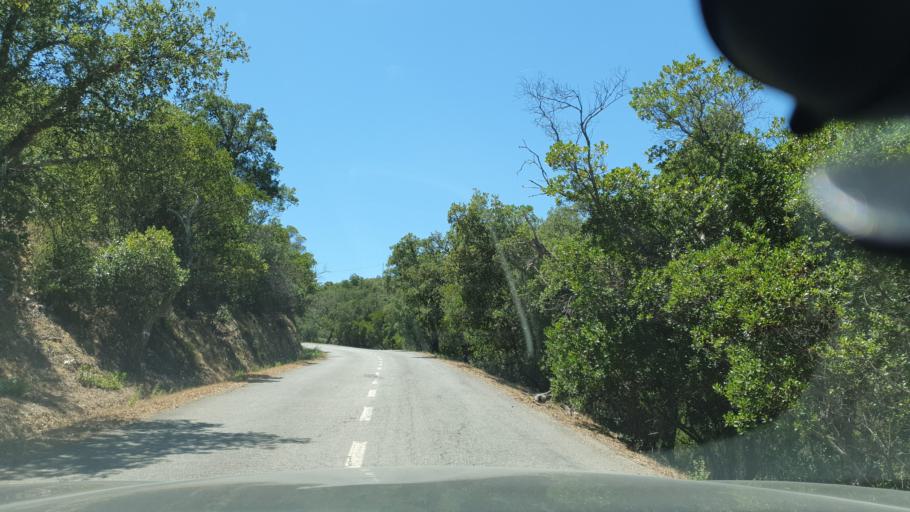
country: PT
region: Beja
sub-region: Odemira
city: Odemira
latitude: 37.6076
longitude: -8.4975
